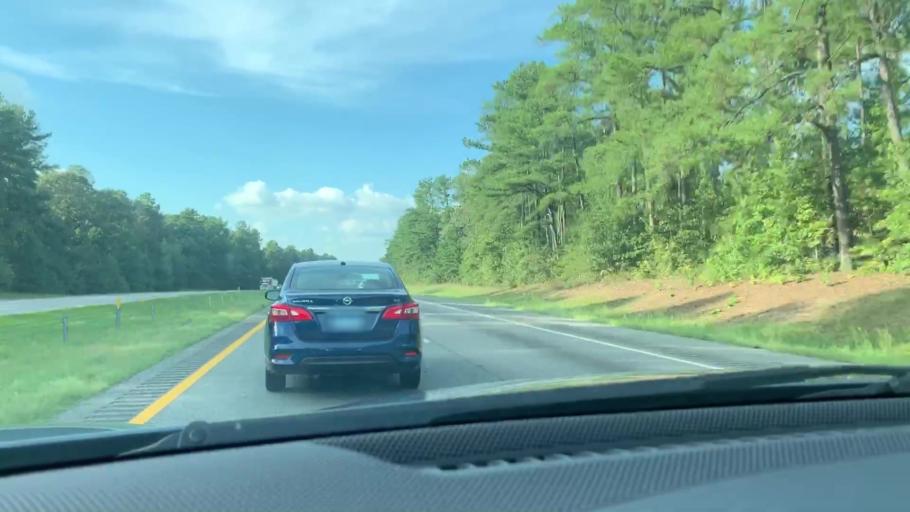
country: US
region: South Carolina
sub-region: Orangeburg County
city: Brookdale
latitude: 33.6017
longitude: -80.8599
